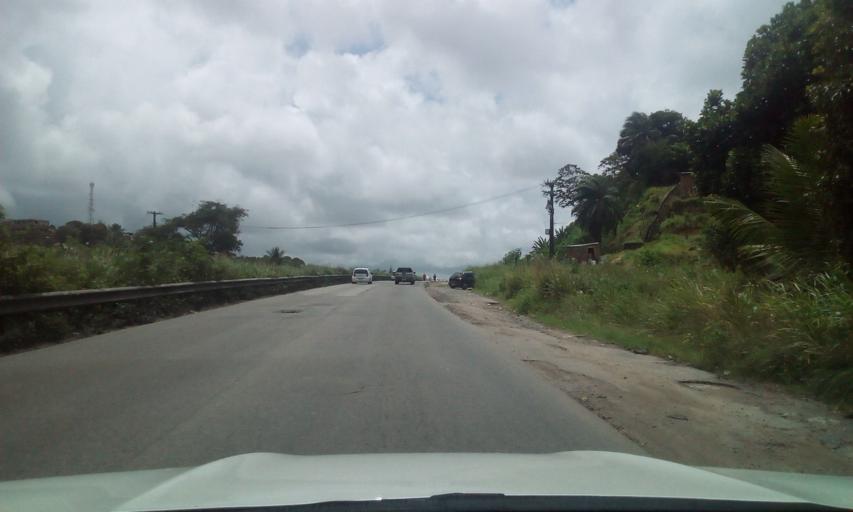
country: BR
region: Pernambuco
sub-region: Jaboatao Dos Guararapes
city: Jaboatao dos Guararapes
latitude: -8.1255
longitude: -34.9438
